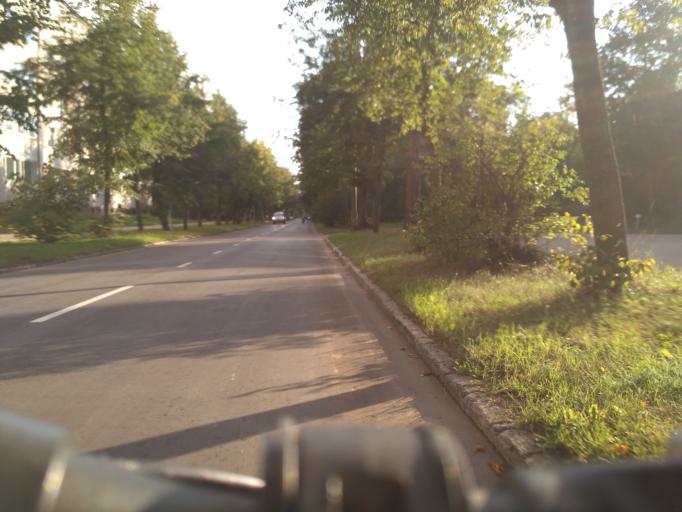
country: RU
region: Moskovskaya
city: Dubna
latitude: 56.7510
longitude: 37.1986
